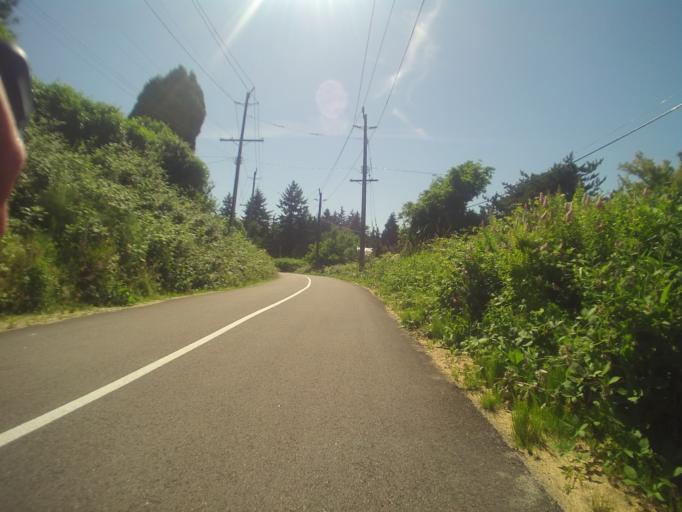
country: CA
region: British Columbia
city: Vancouver
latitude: 49.2409
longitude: -123.1532
